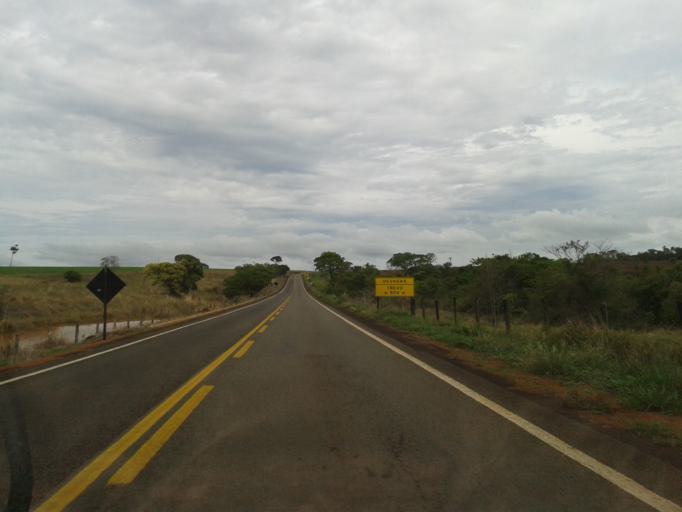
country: BR
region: Goias
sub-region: Buriti Alegre
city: Buriti Alegre
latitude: -18.1517
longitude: -48.9569
